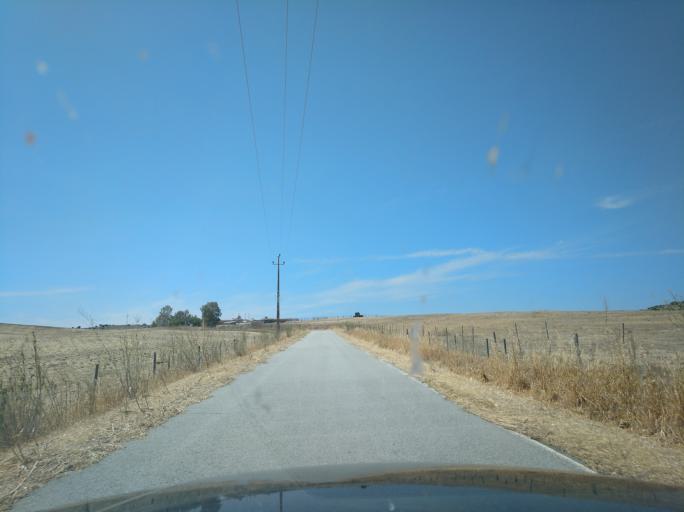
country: PT
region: Portalegre
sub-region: Campo Maior
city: Campo Maior
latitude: 38.9620
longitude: -7.1111
